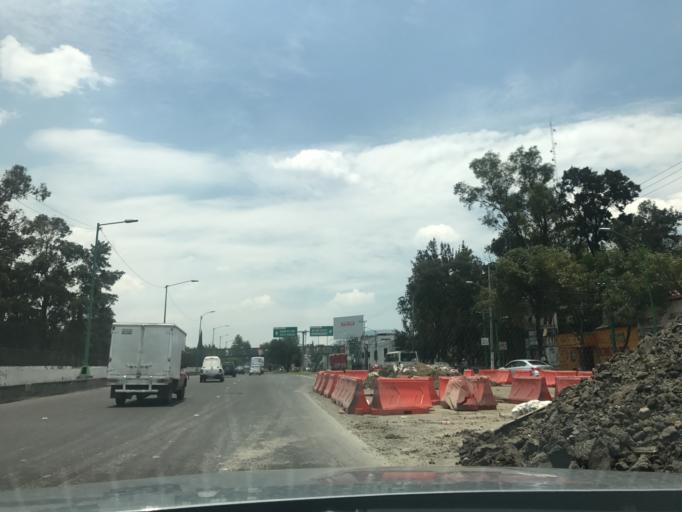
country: MX
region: Mexico
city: Colonia Lindavista
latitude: 19.4948
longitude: -99.1466
